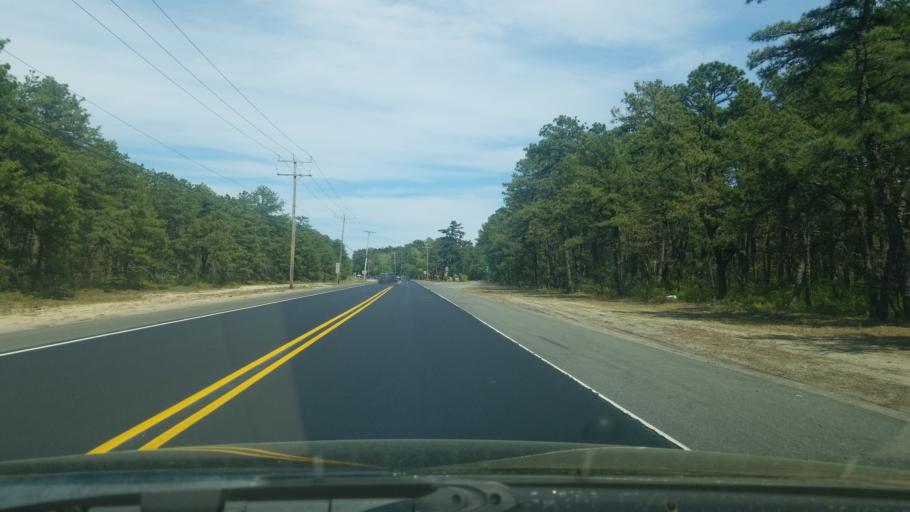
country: US
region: New Jersey
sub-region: Ocean County
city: Lakehurst
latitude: 40.0066
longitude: -74.3355
